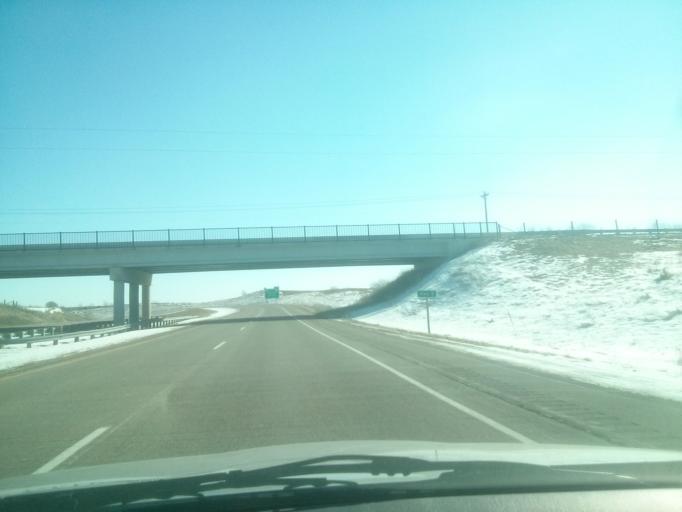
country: US
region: Wisconsin
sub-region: Saint Croix County
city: Somerset
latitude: 45.1088
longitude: -92.6762
